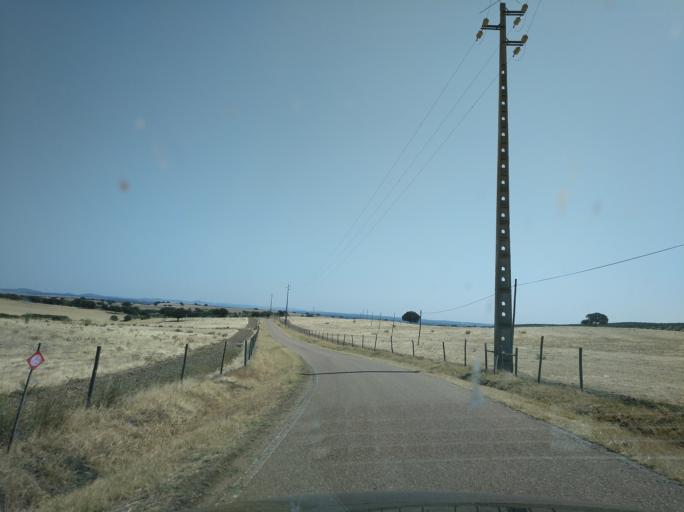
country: PT
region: Portalegre
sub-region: Campo Maior
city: Campo Maior
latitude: 39.0270
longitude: -7.0252
